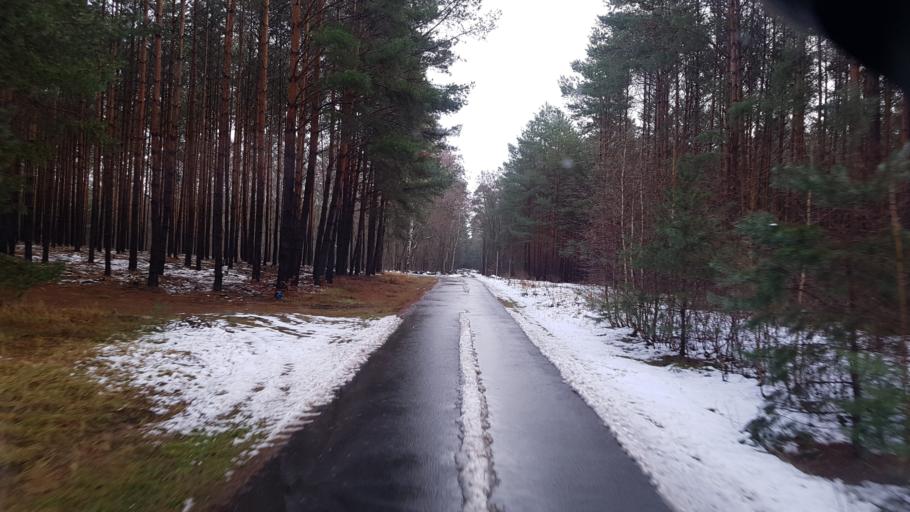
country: DE
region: Brandenburg
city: Straupitz
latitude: 51.9633
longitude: 14.1647
